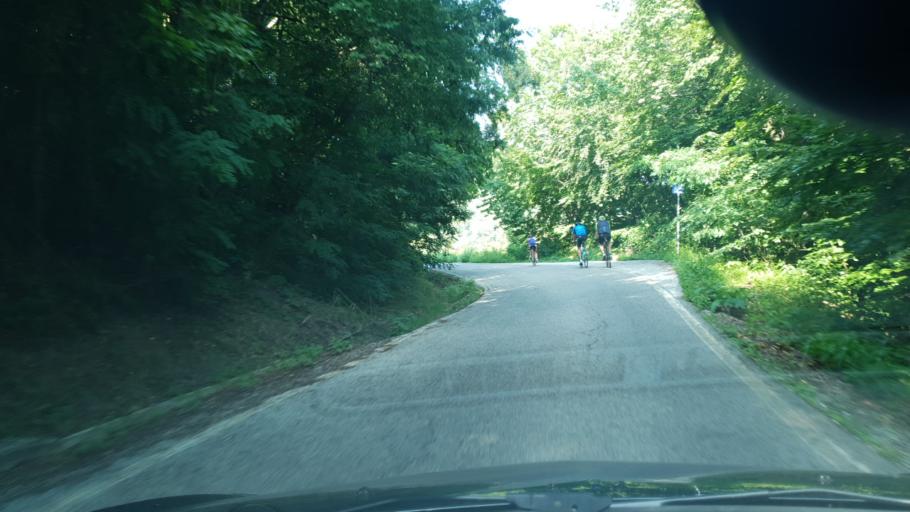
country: HR
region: Grad Zagreb
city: Kasina
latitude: 45.8824
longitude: 15.9753
